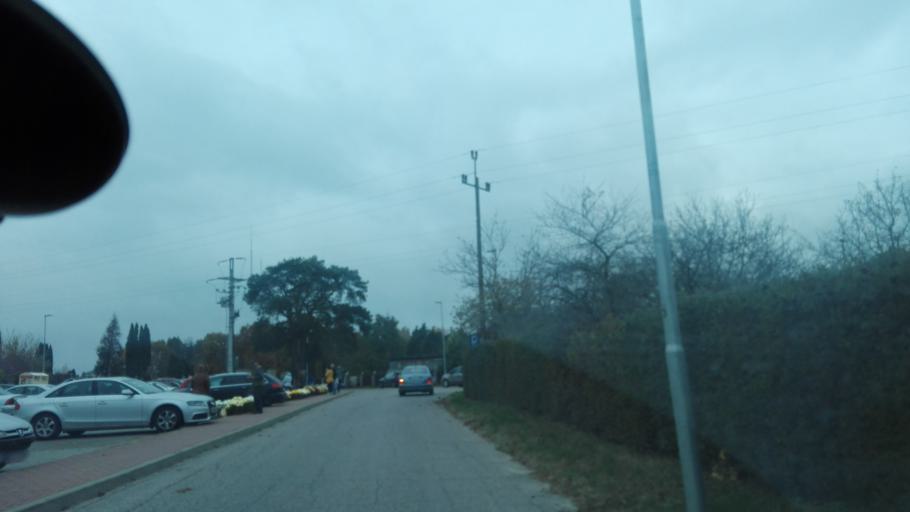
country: PL
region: Lublin Voivodeship
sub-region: Powiat pulawski
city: Pulawy
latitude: 51.4102
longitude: 21.9245
